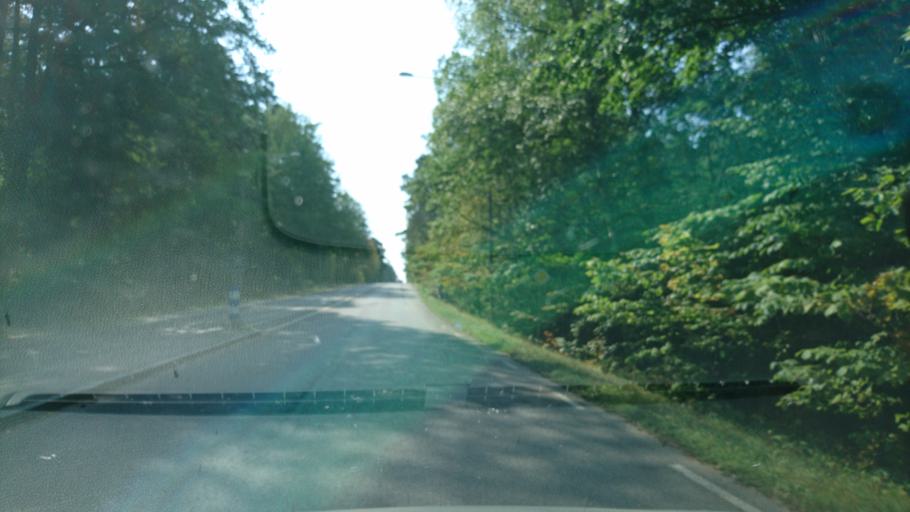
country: SE
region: Uppsala
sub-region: Uppsala Kommun
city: Uppsala
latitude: 59.8317
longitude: 17.6428
